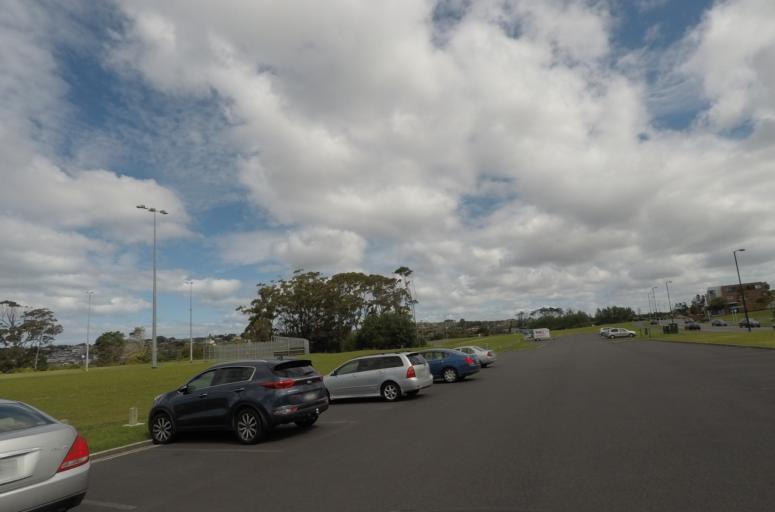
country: NZ
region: Auckland
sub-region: Auckland
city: Rothesay Bay
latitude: -36.6016
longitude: 174.6792
